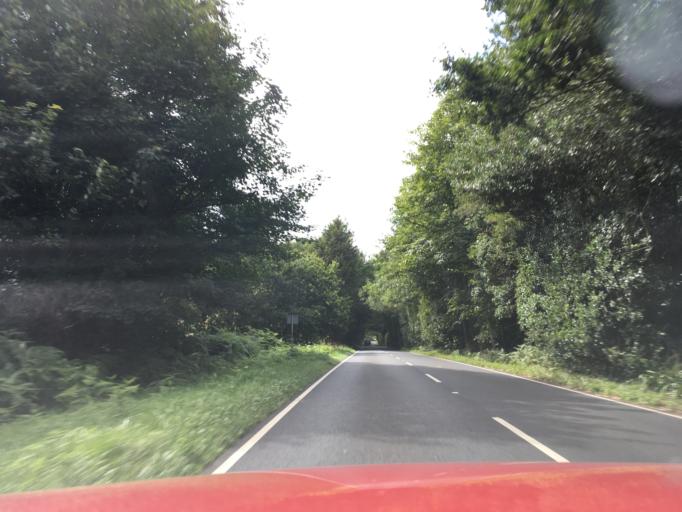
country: GB
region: England
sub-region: Kent
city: Edenbridge
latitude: 51.1339
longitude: 0.0822
